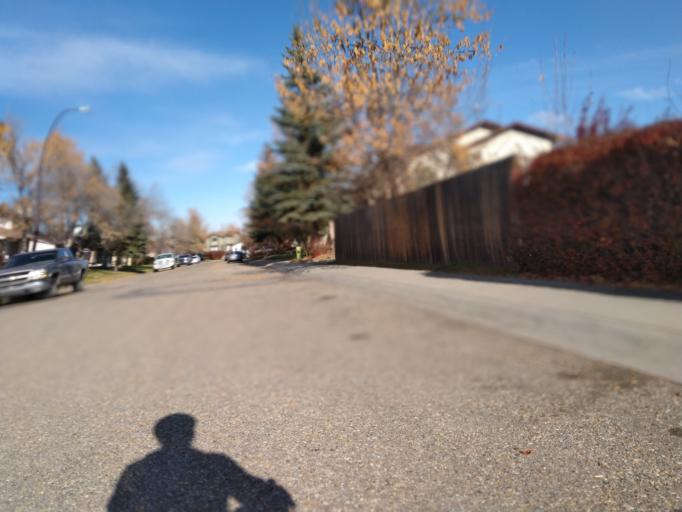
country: CA
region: Alberta
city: Calgary
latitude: 51.1257
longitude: -114.0886
